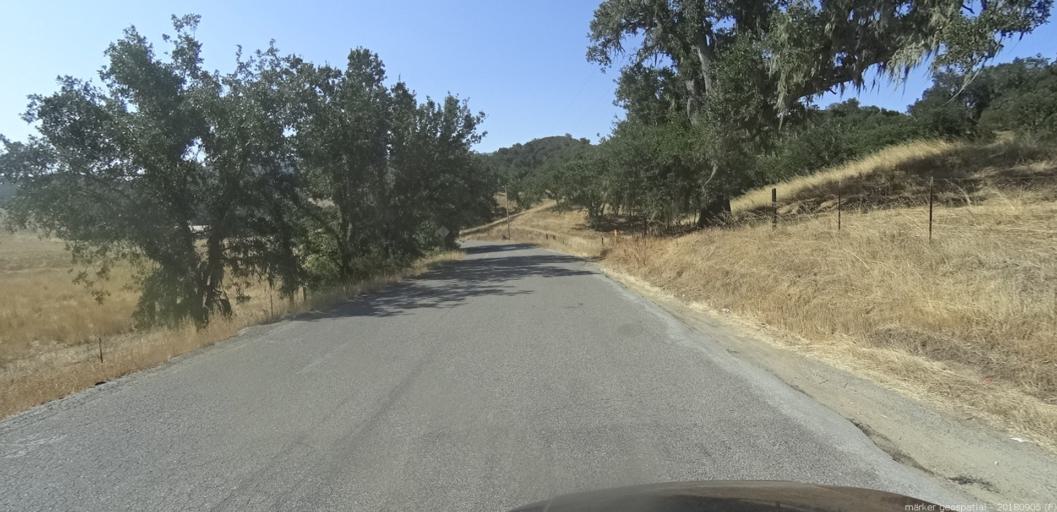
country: US
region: California
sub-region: Monterey County
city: Gonzales
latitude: 36.4013
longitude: -121.5809
